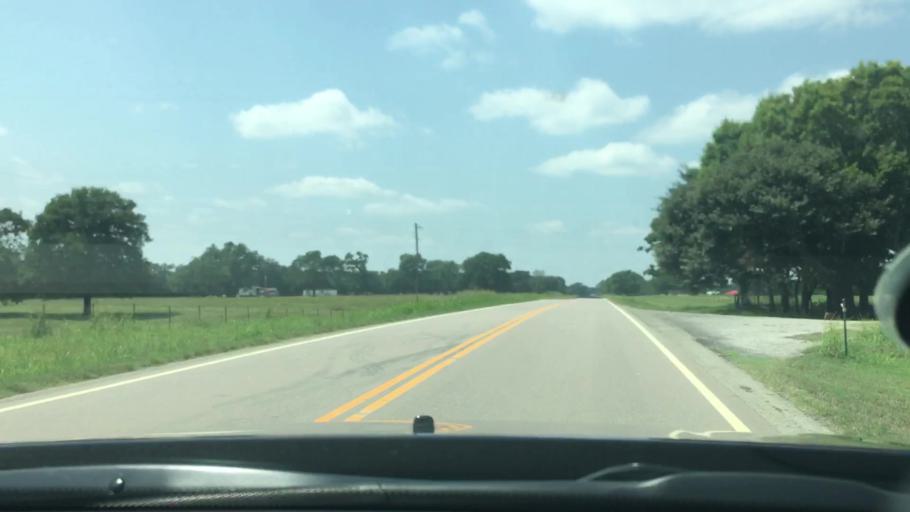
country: US
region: Oklahoma
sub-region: Coal County
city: Coalgate
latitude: 34.3688
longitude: -96.3422
